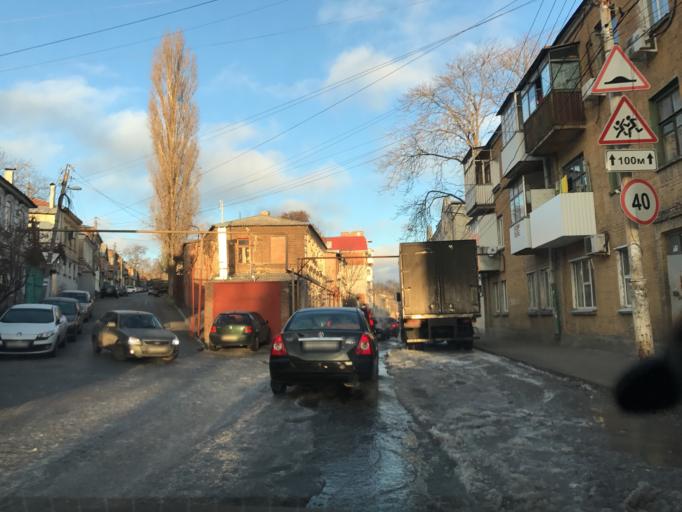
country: RU
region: Rostov
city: Rostov-na-Donu
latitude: 47.2170
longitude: 39.6865
